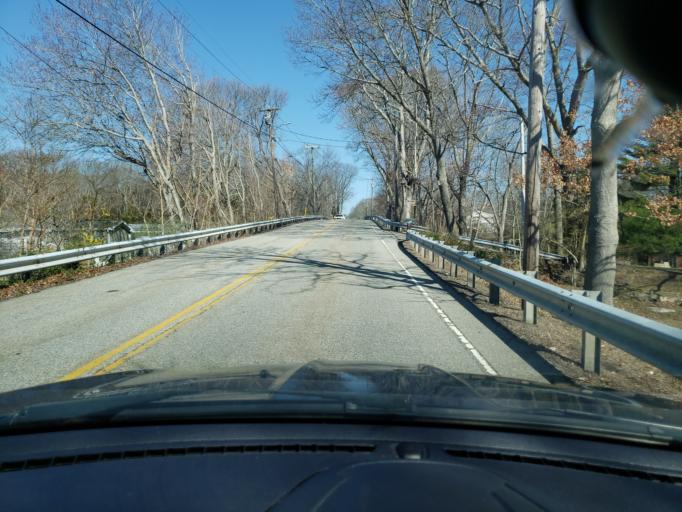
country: US
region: Connecticut
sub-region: Middlesex County
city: Westbrook Center
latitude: 41.2767
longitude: -72.4849
